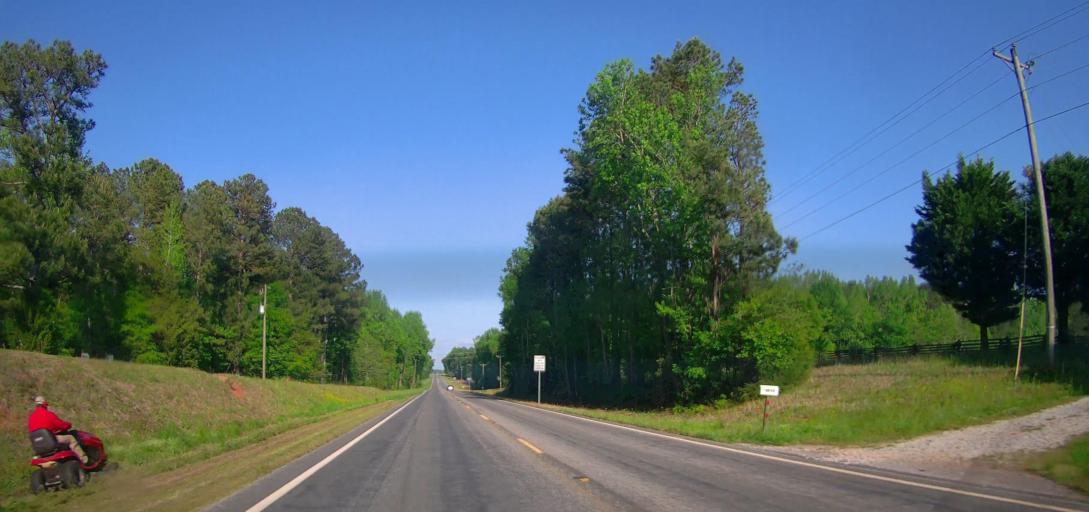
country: US
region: Georgia
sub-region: Walton County
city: Social Circle
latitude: 33.6254
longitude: -83.6491
